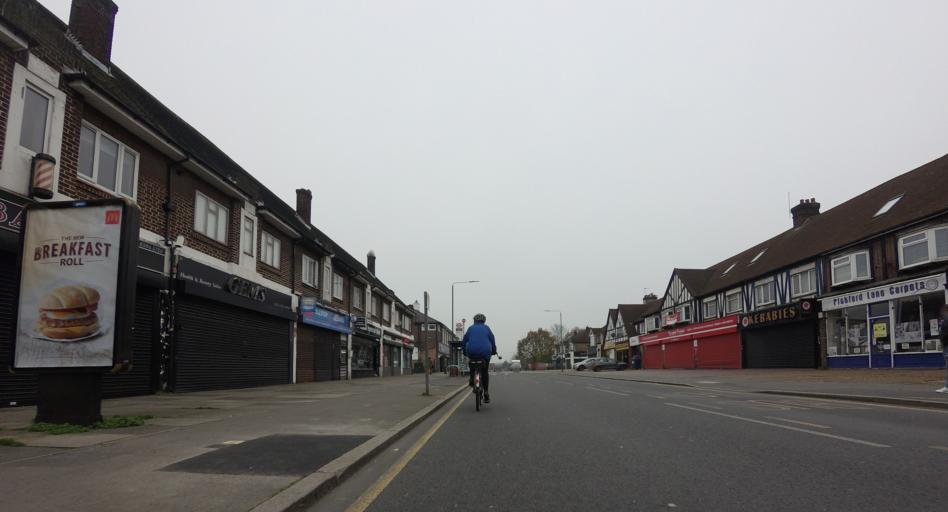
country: GB
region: England
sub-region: Greater London
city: Bexleyheath
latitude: 51.4647
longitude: 0.1330
